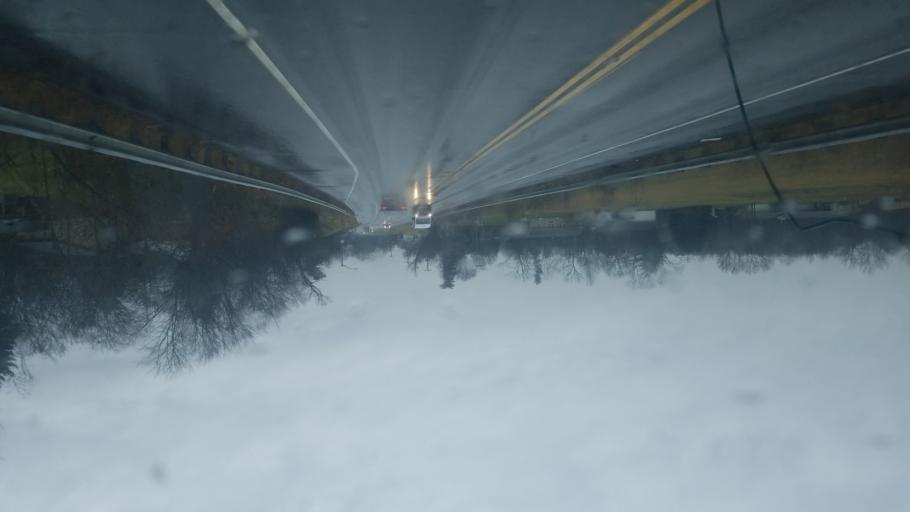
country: US
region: Indiana
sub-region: Bartholomew County
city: Columbus
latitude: 39.1995
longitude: -85.9760
